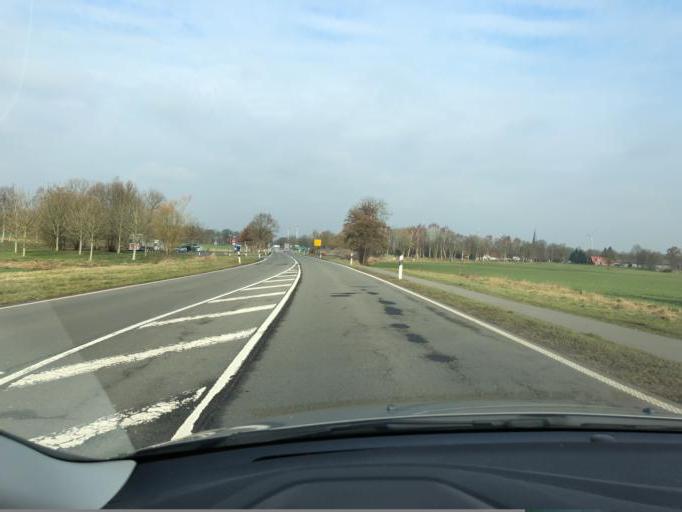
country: DE
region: Lower Saxony
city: Hesel
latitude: 53.3420
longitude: 7.6069
